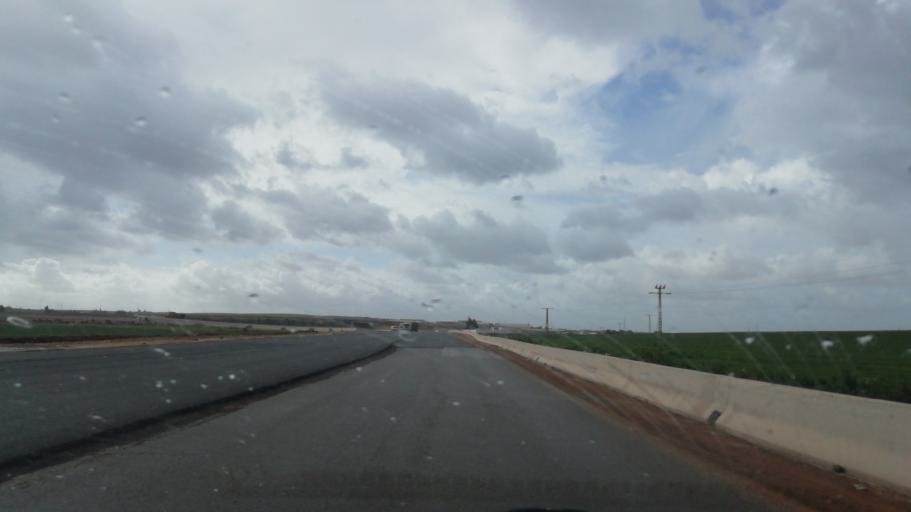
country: DZ
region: Oran
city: Sidi ech Chahmi
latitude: 35.6466
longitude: -0.5246
